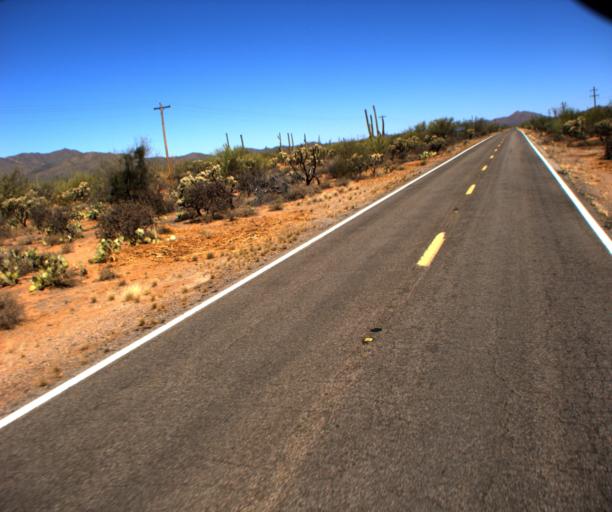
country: US
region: Arizona
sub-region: Pima County
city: Sells
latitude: 32.1198
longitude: -112.0813
